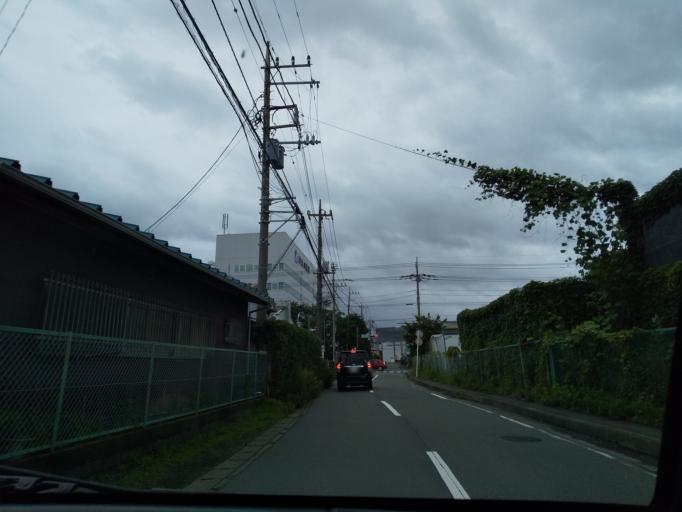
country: JP
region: Kanagawa
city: Minami-rinkan
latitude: 35.4403
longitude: 139.4388
